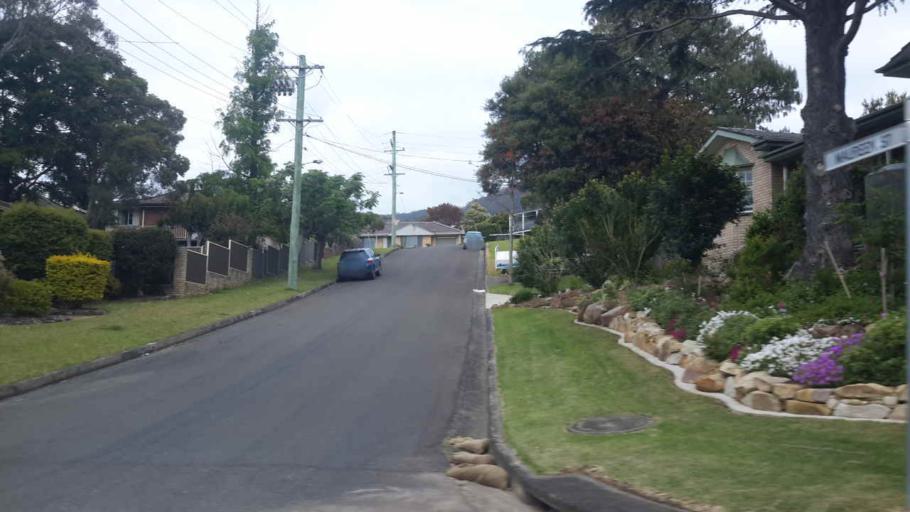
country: AU
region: New South Wales
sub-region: Wollongong
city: Bulli
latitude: -34.3140
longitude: 150.9104
